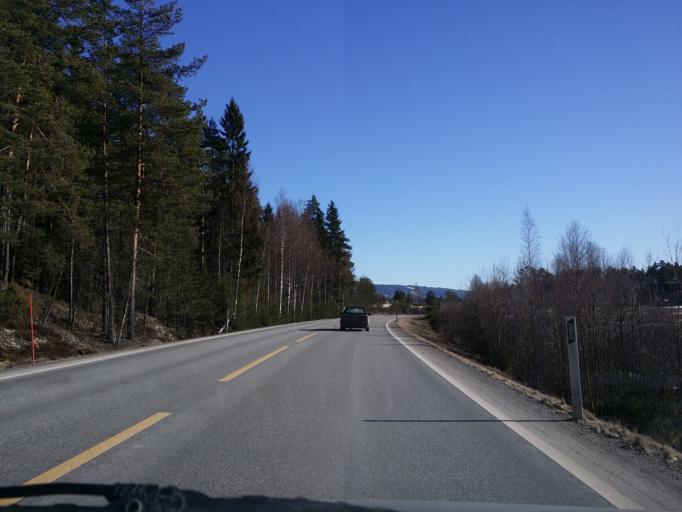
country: NO
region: Buskerud
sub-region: Ringerike
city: Honefoss
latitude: 60.2247
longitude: 10.2536
